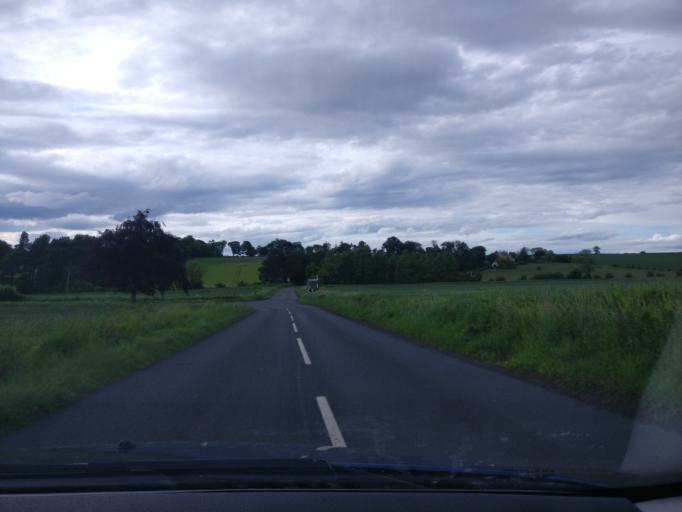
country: GB
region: Scotland
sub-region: East Lothian
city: Haddington
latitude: 55.9379
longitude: -2.7523
